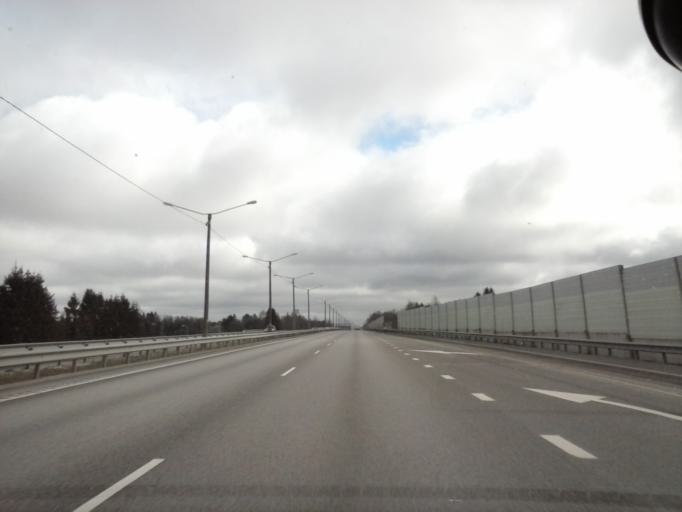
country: EE
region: Harju
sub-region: Rae vald
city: Jueri
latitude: 59.3795
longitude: 24.8417
